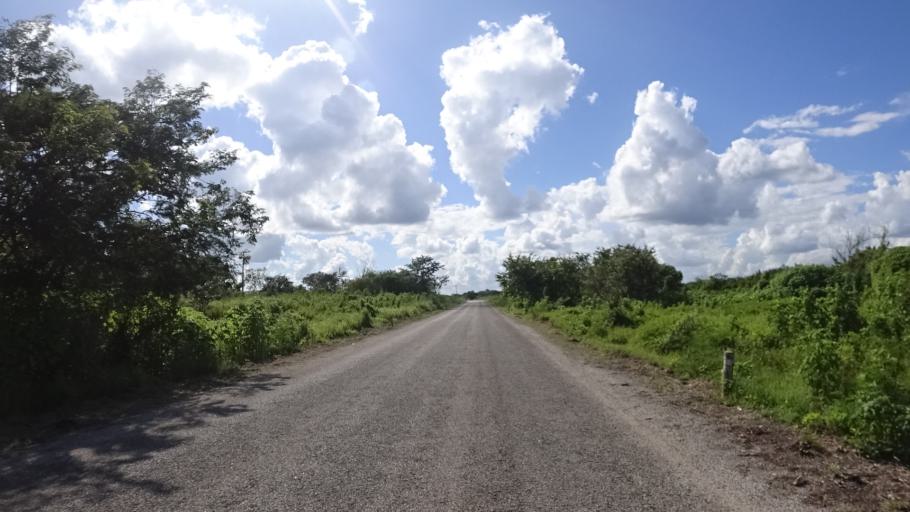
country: MX
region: Yucatan
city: Muna
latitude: 20.6476
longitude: -89.7035
